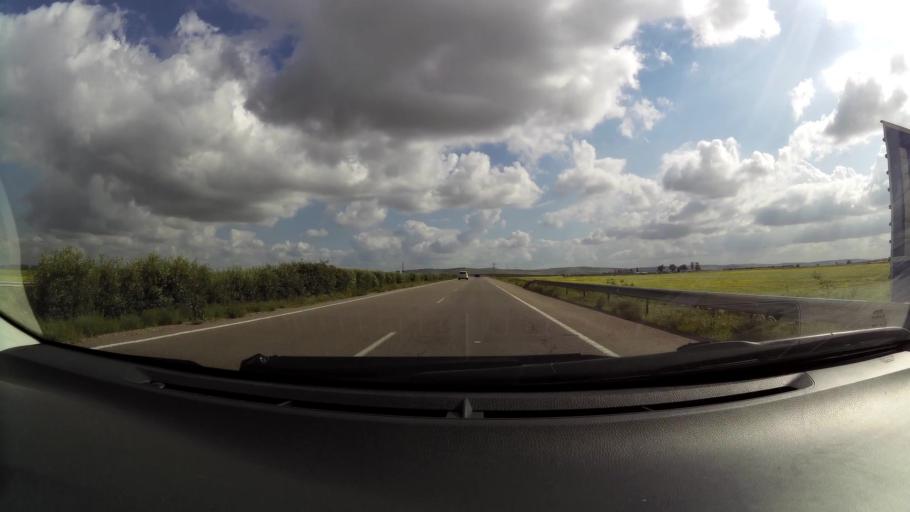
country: MA
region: Chaouia-Ouardigha
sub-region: Settat Province
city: Settat
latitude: 33.1230
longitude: -7.5799
